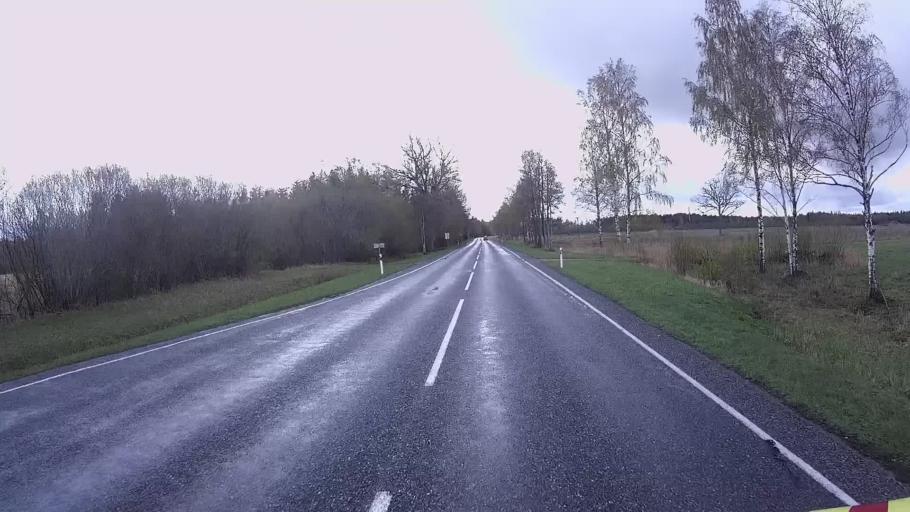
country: EE
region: Hiiumaa
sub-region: Kaerdla linn
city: Kardla
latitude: 58.9213
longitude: 22.9230
